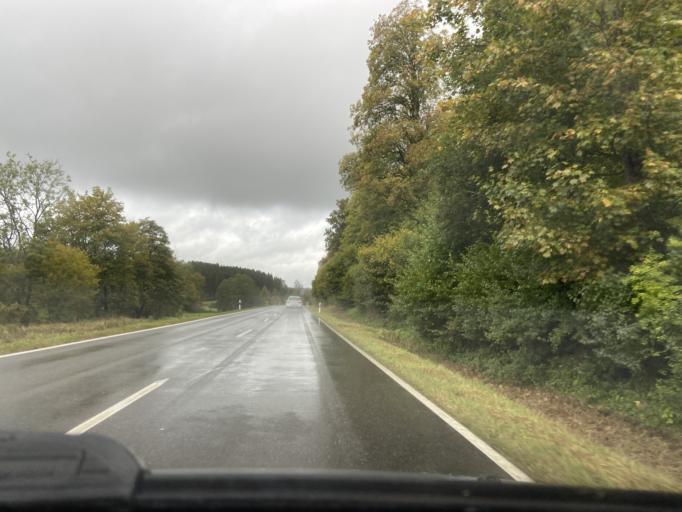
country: DE
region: Baden-Wuerttemberg
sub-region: Tuebingen Region
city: Bingen
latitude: 48.0933
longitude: 9.2820
